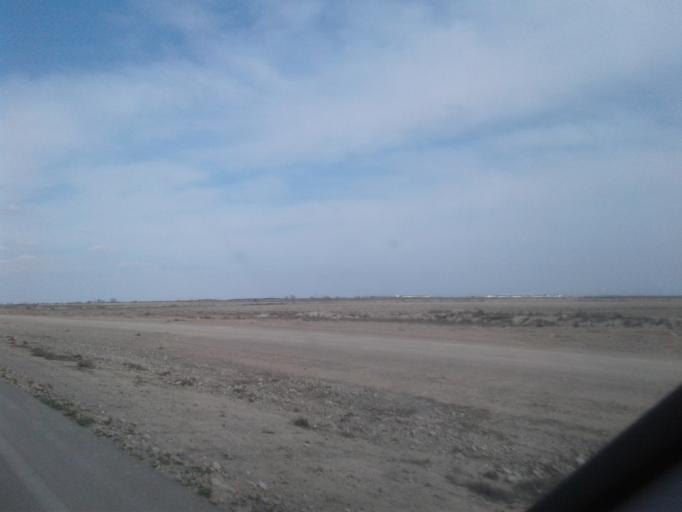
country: TM
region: Ahal
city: Ashgabat
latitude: 38.1948
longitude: 58.4000
